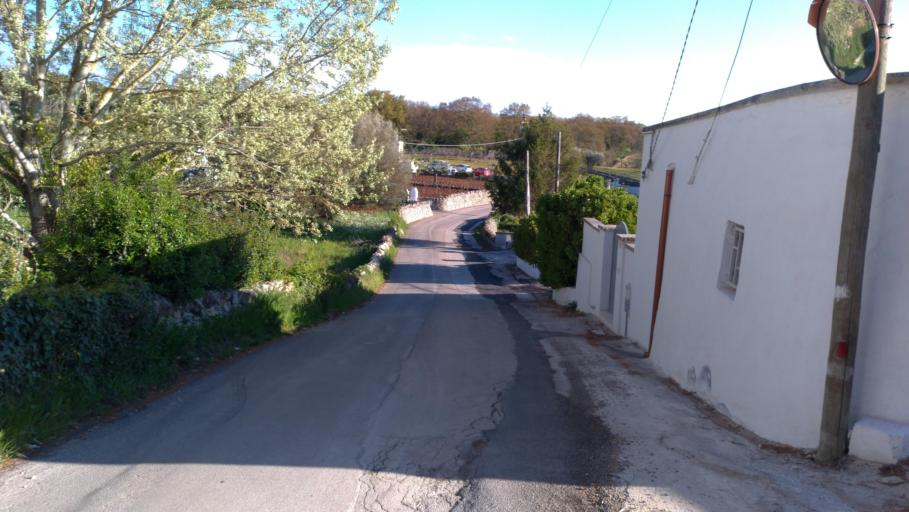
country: IT
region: Apulia
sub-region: Provincia di Taranto
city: Martina Franca
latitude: 40.6930
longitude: 17.3395
